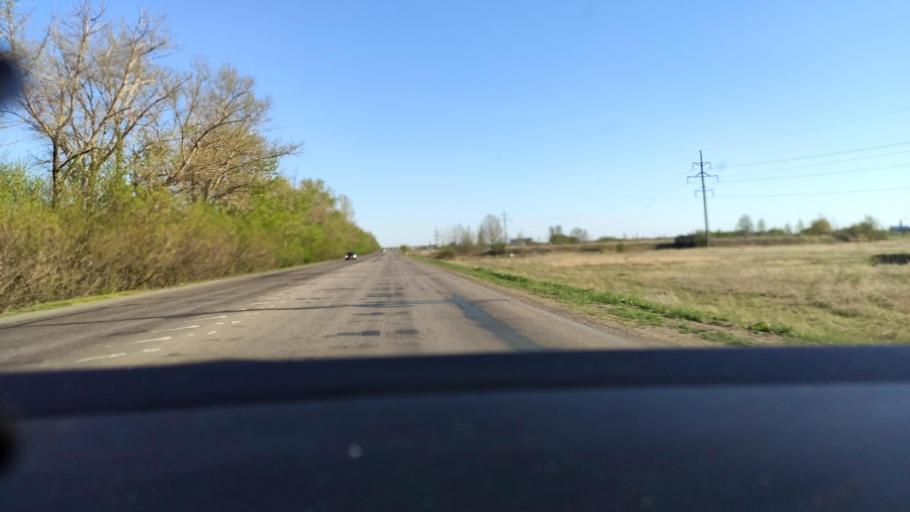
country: RU
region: Voronezj
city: Maslovka
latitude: 51.5141
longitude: 39.3022
